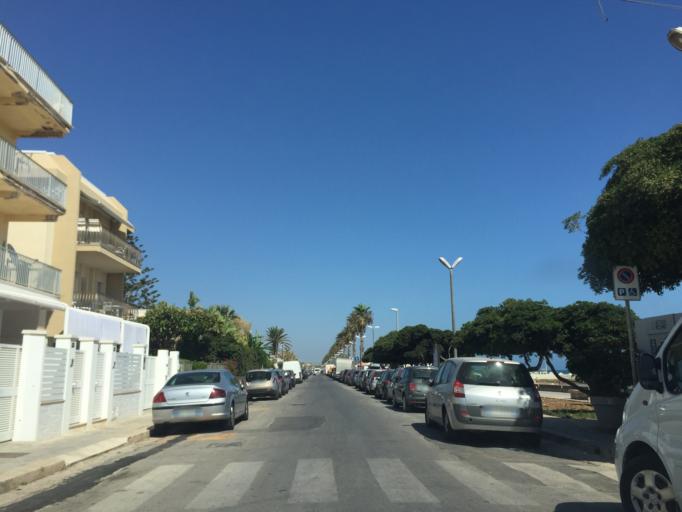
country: IT
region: Sicily
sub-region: Ragusa
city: Marina di Ragusa
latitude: 36.7820
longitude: 14.5598
